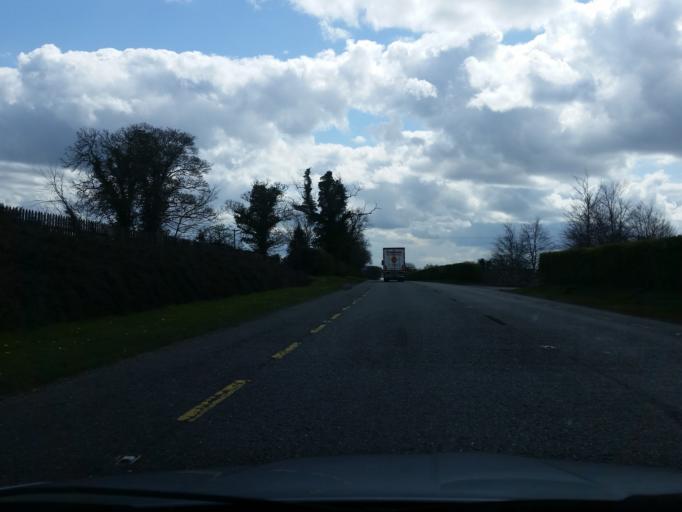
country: IE
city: Kentstown
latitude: 53.6159
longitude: -6.4810
